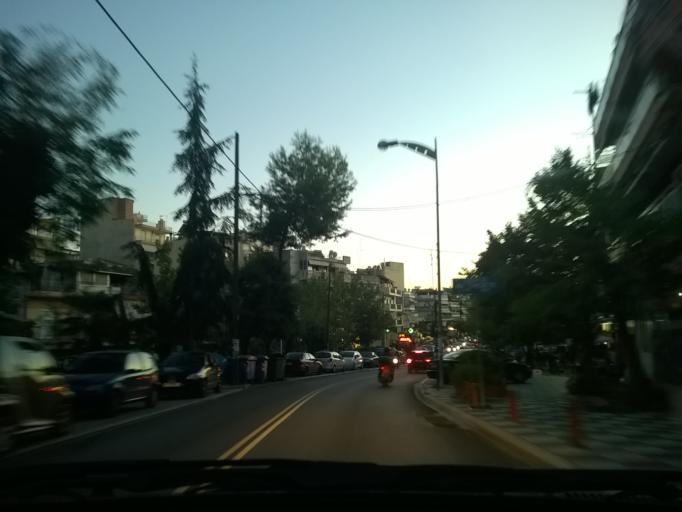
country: GR
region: Central Macedonia
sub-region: Nomos Thessalonikis
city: Polichni
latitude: 40.6602
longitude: 22.9452
